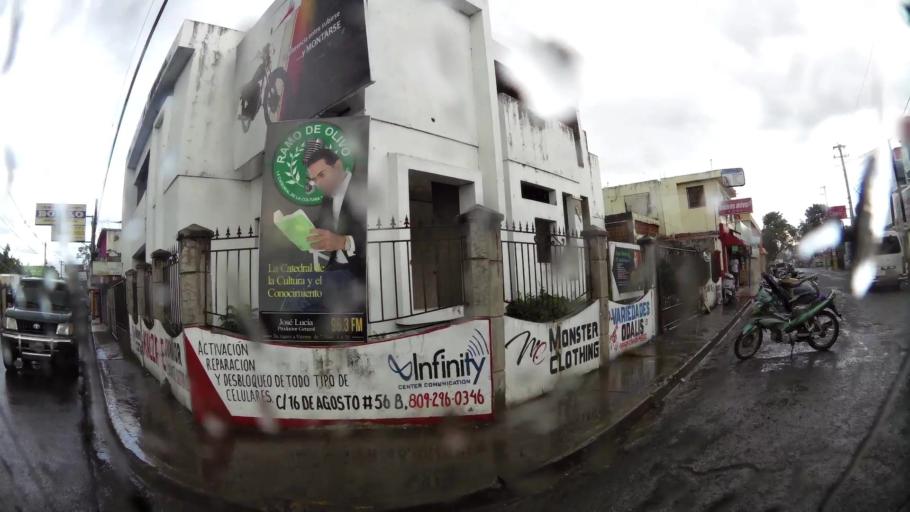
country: DO
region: Monsenor Nouel
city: Bonao
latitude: 18.9402
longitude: -70.4123
